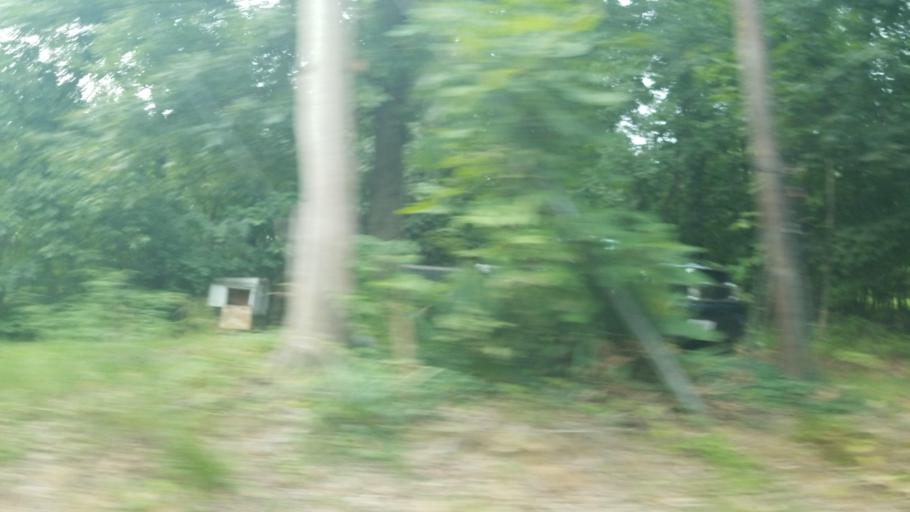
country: US
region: Illinois
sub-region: Saline County
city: Harrisburg
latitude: 37.8478
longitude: -88.6119
